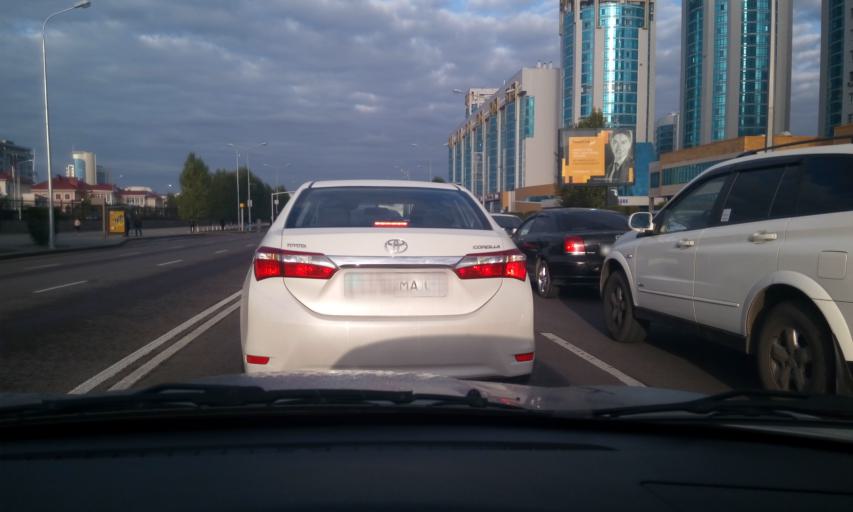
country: KZ
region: Astana Qalasy
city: Astana
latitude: 51.1346
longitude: 71.4269
